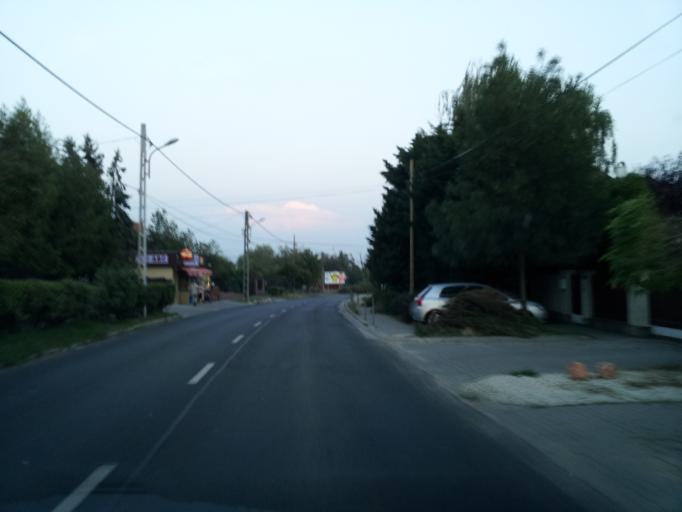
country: HU
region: Budapest
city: Budapest XXII. keruelet
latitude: 47.4278
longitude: 19.0089
